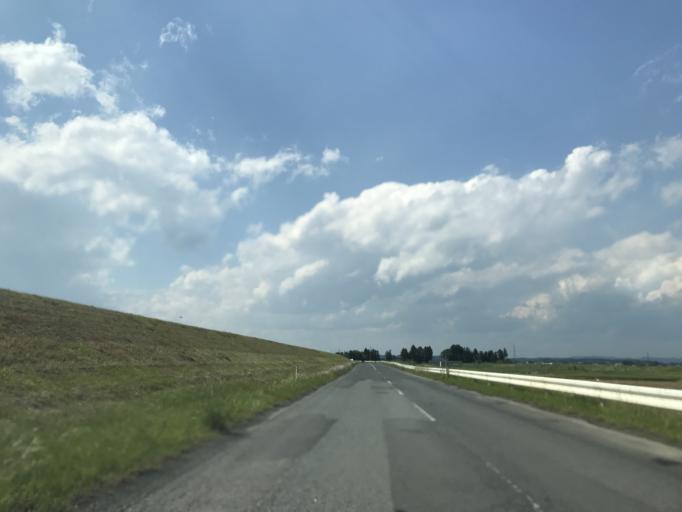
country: JP
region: Miyagi
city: Matsushima
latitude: 38.4398
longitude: 141.1169
